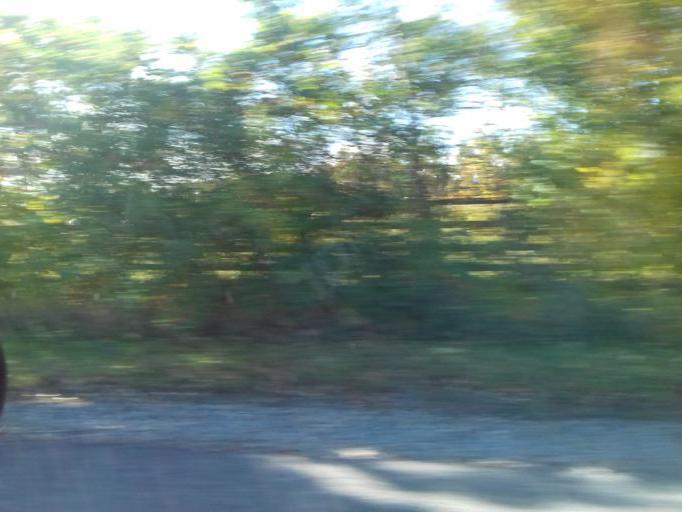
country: IE
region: Leinster
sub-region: An Mhi
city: Ashbourne
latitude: 53.4848
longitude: -6.3791
